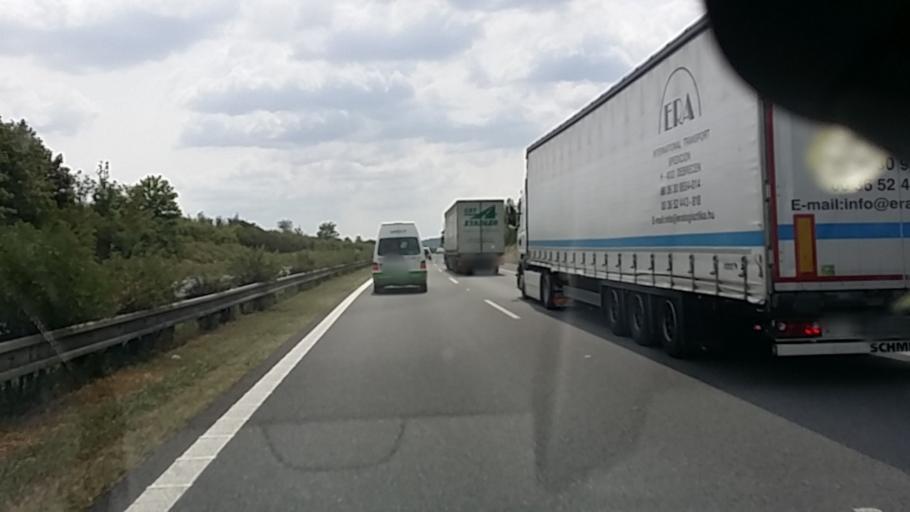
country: CZ
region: Central Bohemia
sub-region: Okres Melnik
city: Veltrusy
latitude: 50.2650
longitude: 14.3660
